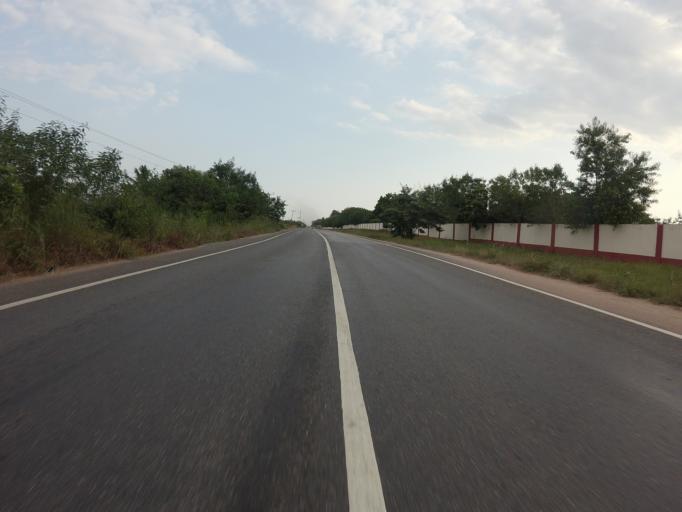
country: GH
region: Volta
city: Anloga
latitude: 6.0966
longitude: 0.5086
